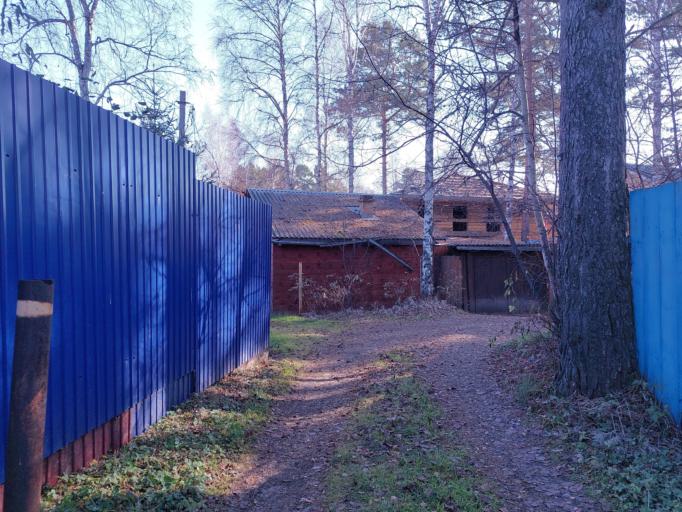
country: RU
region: Irkutsk
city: Pivovarikha
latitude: 52.1873
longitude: 104.4618
